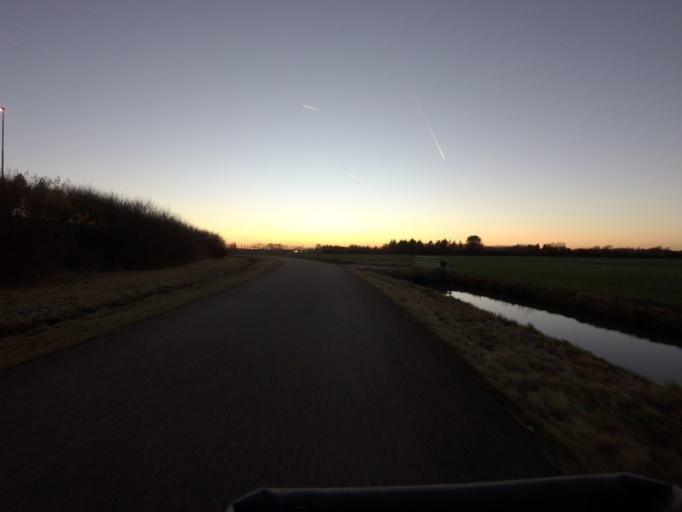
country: NL
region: Utrecht
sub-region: Gemeente Montfoort
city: Montfoort
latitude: 52.0840
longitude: 4.9787
